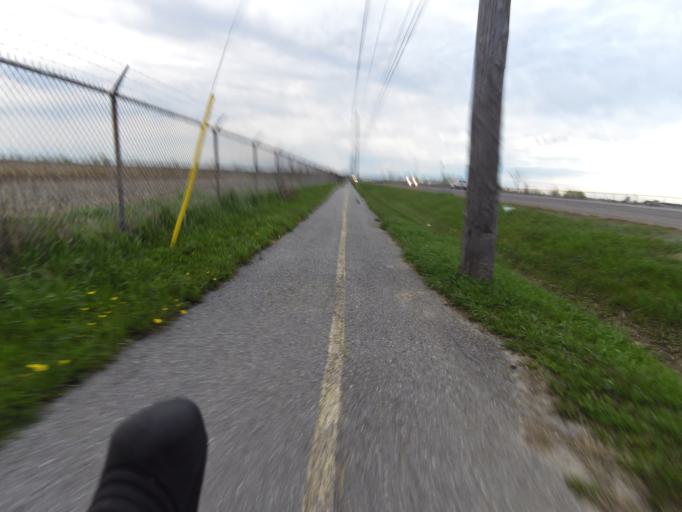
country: CA
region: Ontario
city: Bells Corners
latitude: 45.2964
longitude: -75.7622
